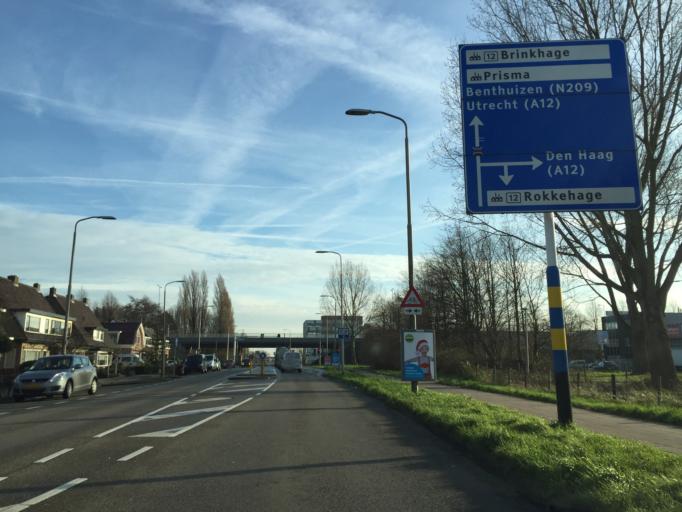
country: NL
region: South Holland
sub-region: Gemeente Zoetermeer
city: Zoetermeer
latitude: 52.0491
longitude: 4.5112
